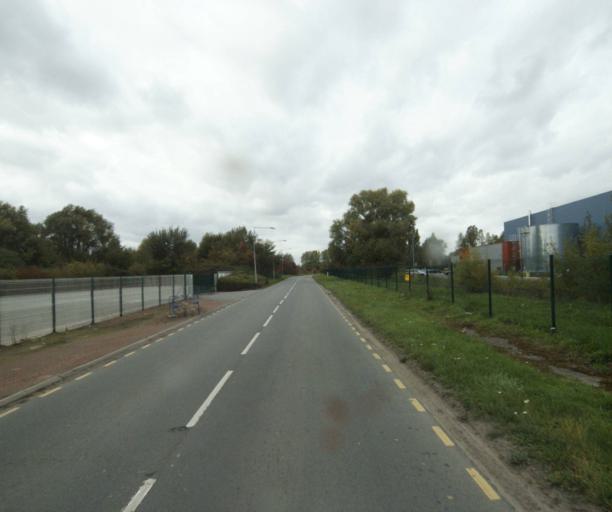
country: FR
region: Nord-Pas-de-Calais
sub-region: Departement du Nord
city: Radinghem-en-Weppes
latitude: 50.6512
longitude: 2.9093
